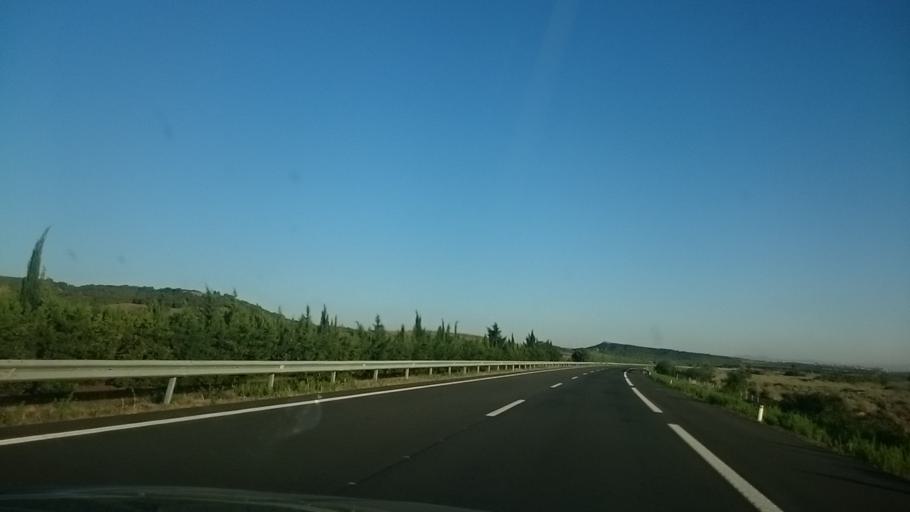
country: ES
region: La Rioja
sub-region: Provincia de La Rioja
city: Aldeanueva de Ebro
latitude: 42.2534
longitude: -1.9170
